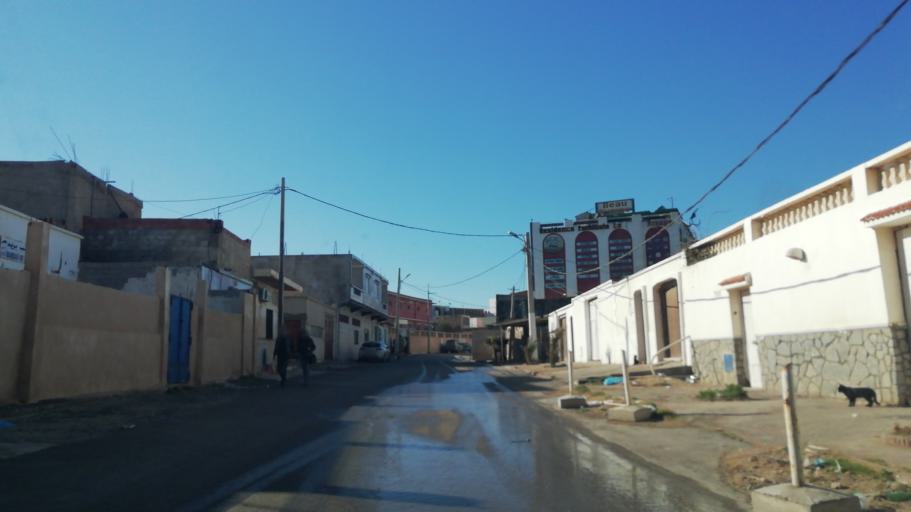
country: DZ
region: Oran
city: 'Ain el Turk
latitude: 35.7241
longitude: -0.8492
